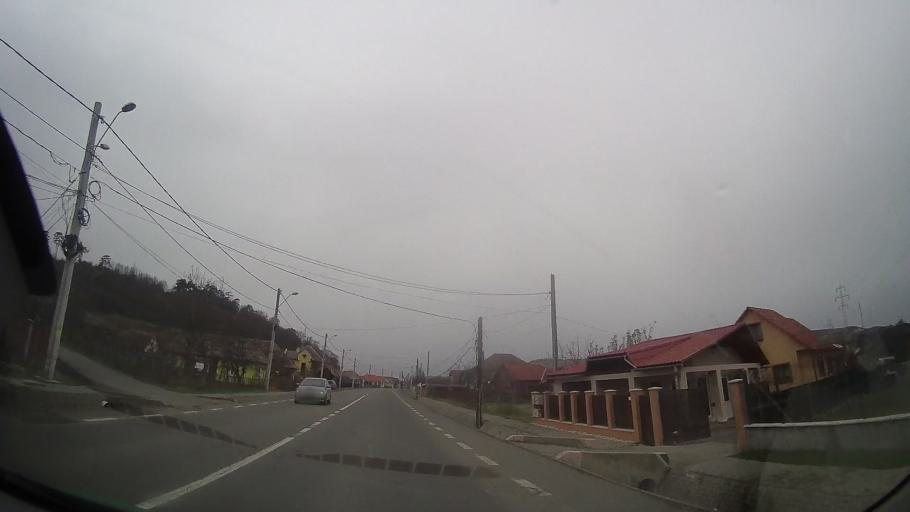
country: RO
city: Remetea
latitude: 46.5960
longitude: 24.5319
